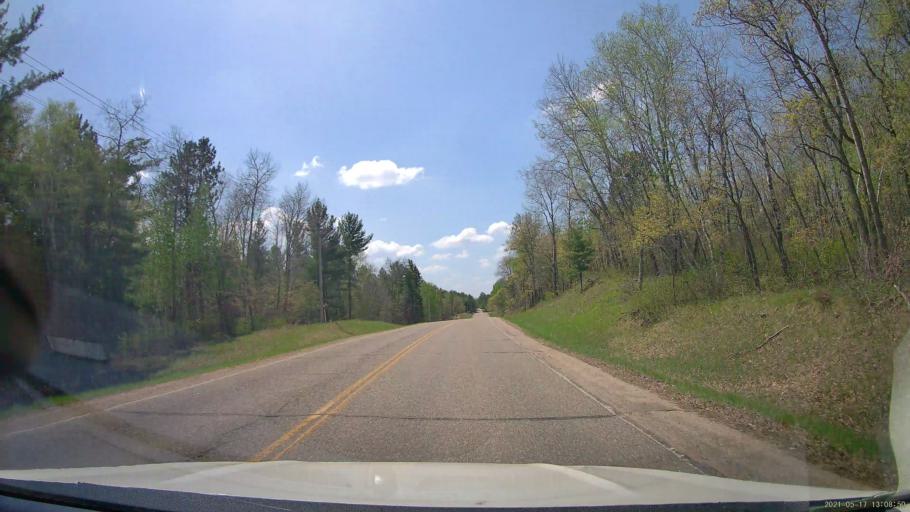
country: US
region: Minnesota
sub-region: Hubbard County
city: Park Rapids
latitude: 47.0331
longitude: -94.9206
